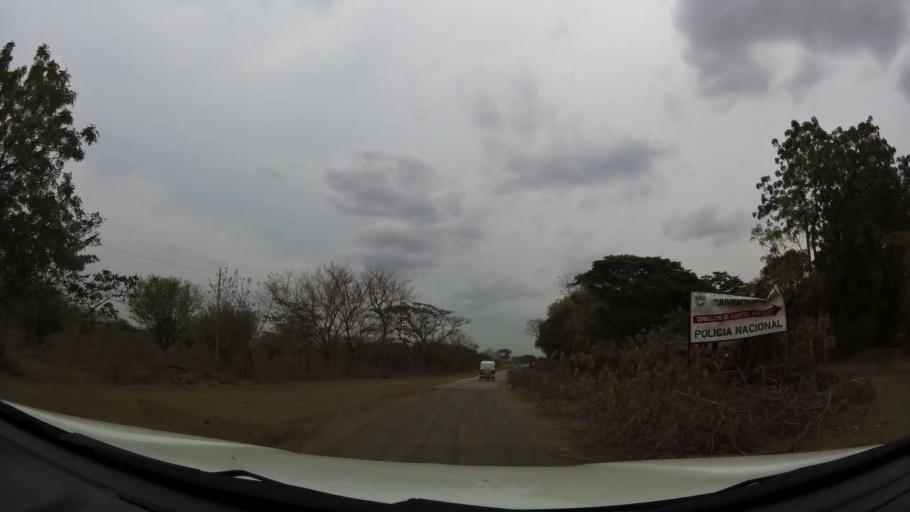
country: NI
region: Masaya
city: Ticuantepe
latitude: 12.0879
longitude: -86.1866
